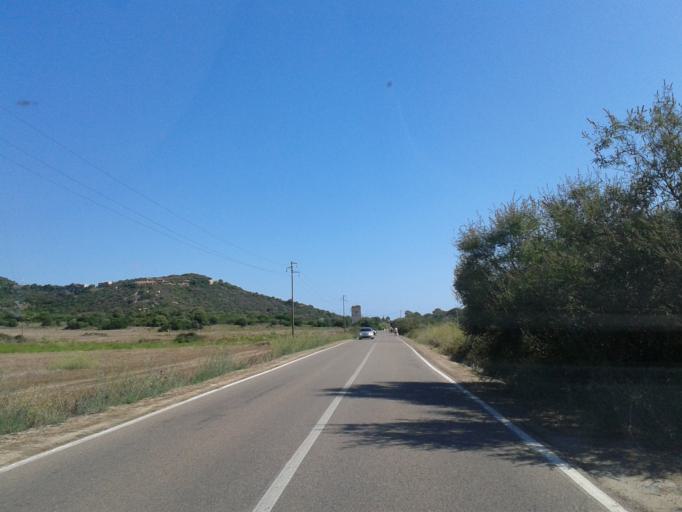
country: IT
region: Sardinia
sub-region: Provincia di Cagliari
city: Olia Speciosa
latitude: 39.2401
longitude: 9.5612
